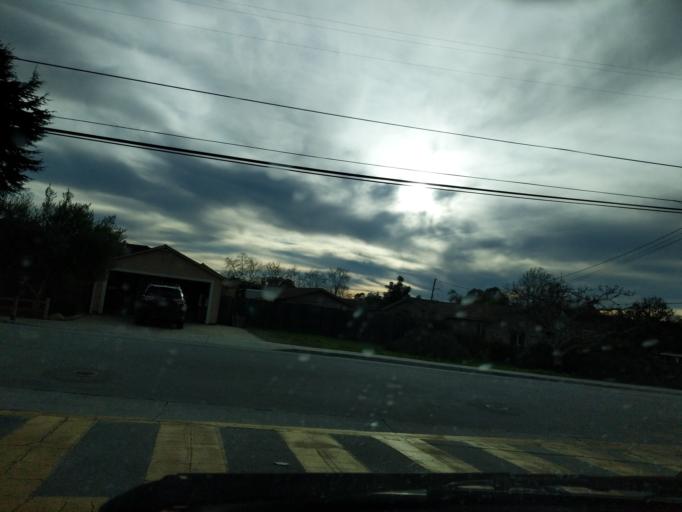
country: US
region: California
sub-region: Santa Cruz County
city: Freedom
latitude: 36.9430
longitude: -121.7920
